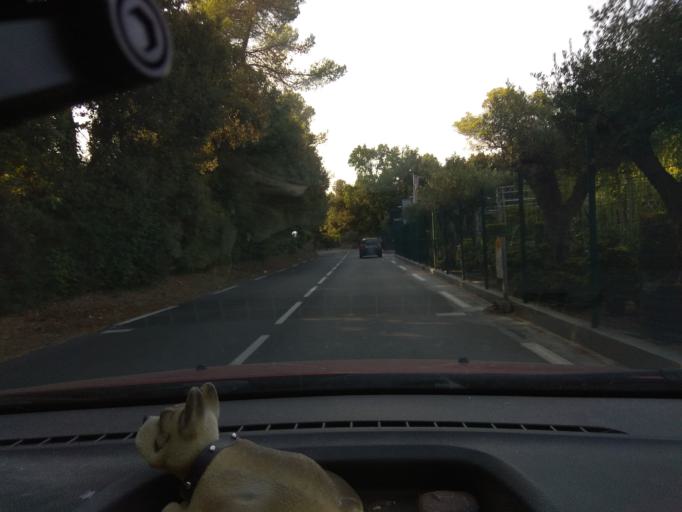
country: FR
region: Provence-Alpes-Cote d'Azur
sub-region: Departement des Alpes-Maritimes
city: Le Rouret
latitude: 43.6533
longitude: 7.0284
